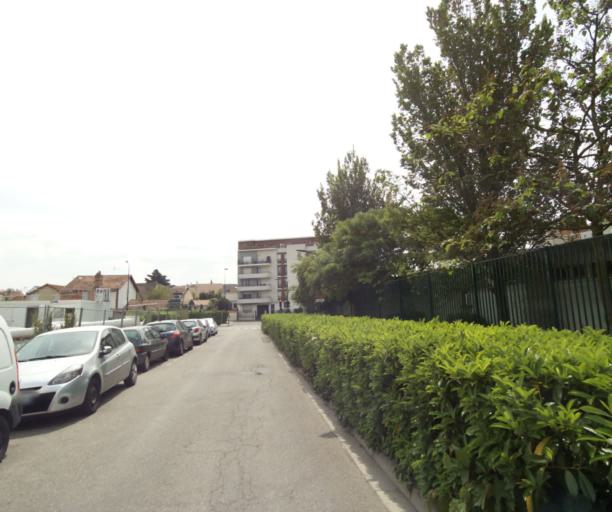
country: FR
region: Ile-de-France
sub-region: Departement du Val-d'Oise
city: Bezons
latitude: 48.9227
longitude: 2.2326
